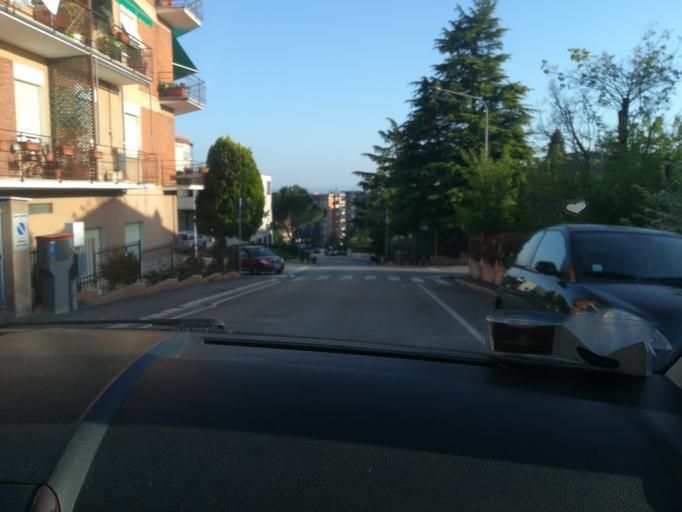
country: IT
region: The Marches
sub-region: Provincia di Macerata
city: Macerata
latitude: 43.2933
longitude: 13.4326
